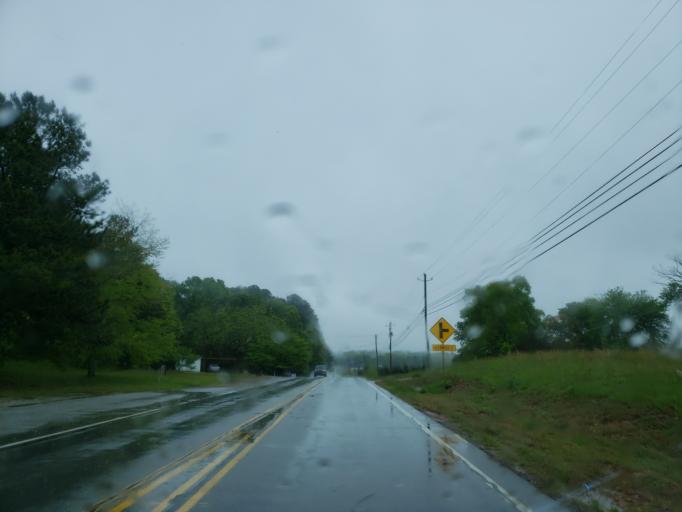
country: US
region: Georgia
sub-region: Haralson County
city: Bremen
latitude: 33.7077
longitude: -85.1690
